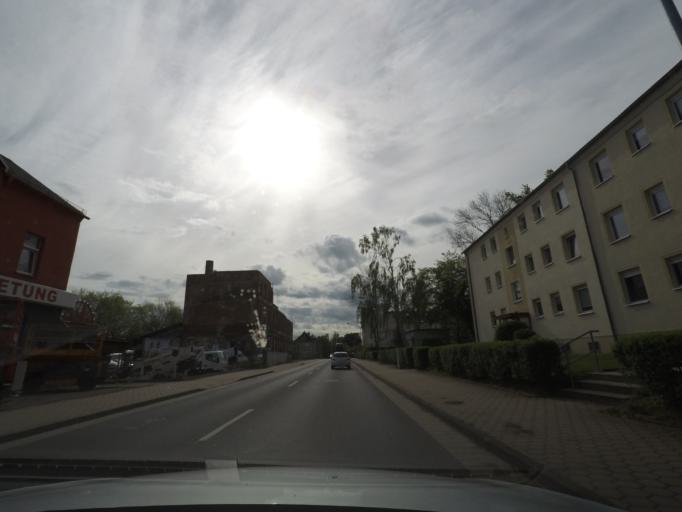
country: DE
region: Saxony
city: Dobeln
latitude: 51.1243
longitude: 13.0985
